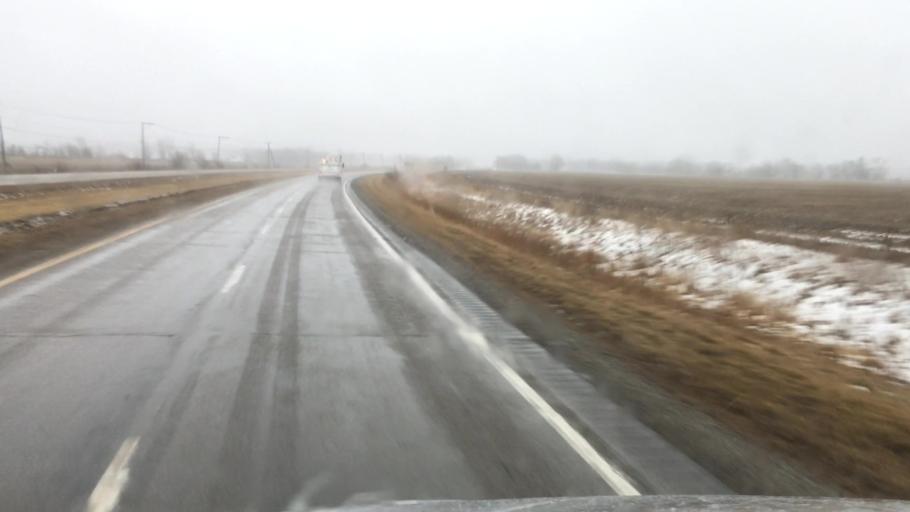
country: US
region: Indiana
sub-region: Newton County
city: Roselawn
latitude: 41.1220
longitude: -87.4495
